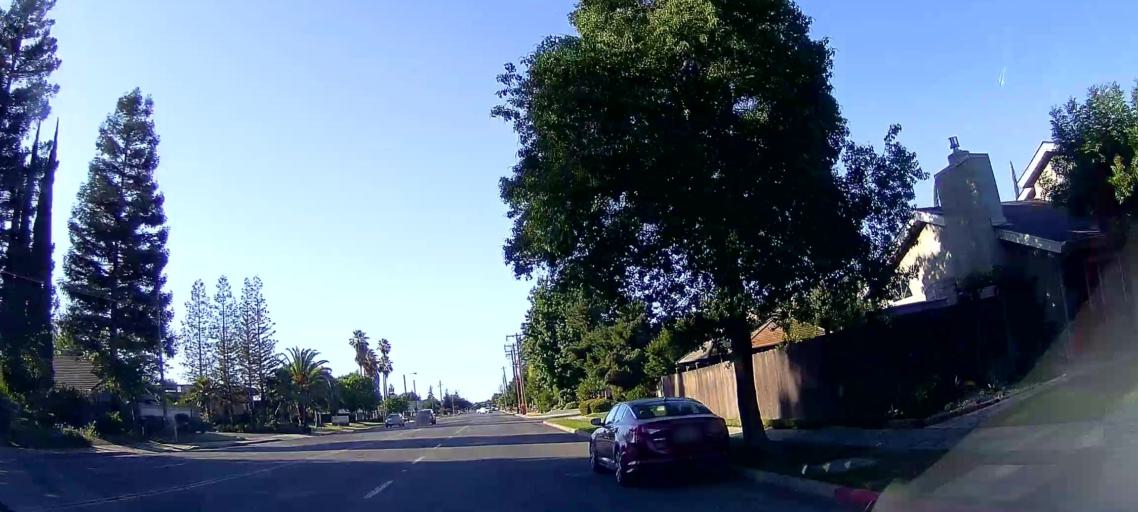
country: US
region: California
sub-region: Fresno County
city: Fresno
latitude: 36.8314
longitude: -119.7993
